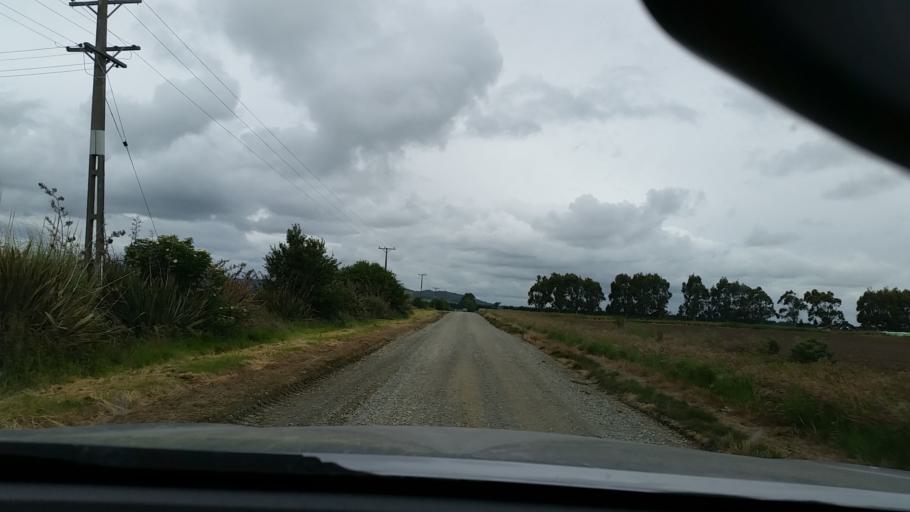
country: NZ
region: Southland
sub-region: Southland District
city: Winton
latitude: -46.2285
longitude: 168.3608
